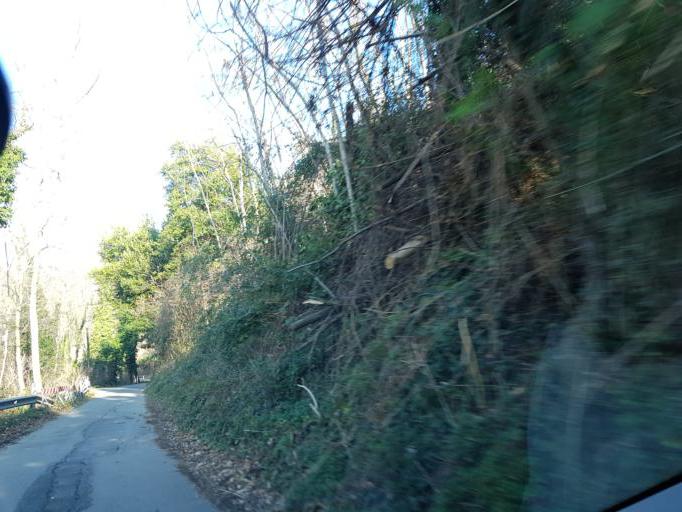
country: IT
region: Liguria
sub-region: Provincia di Genova
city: Santa Marta
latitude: 44.4930
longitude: 8.8868
